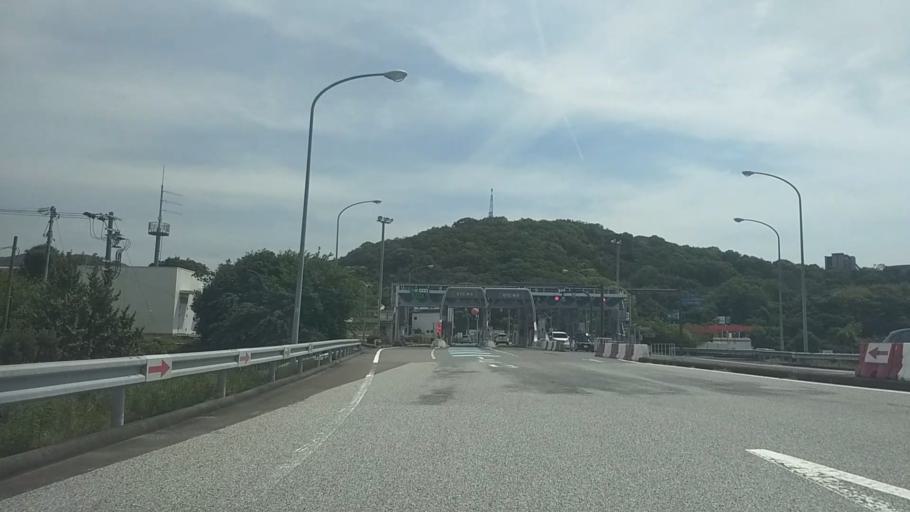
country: JP
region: Shizuoka
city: Kosai-shi
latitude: 34.7978
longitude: 137.5820
